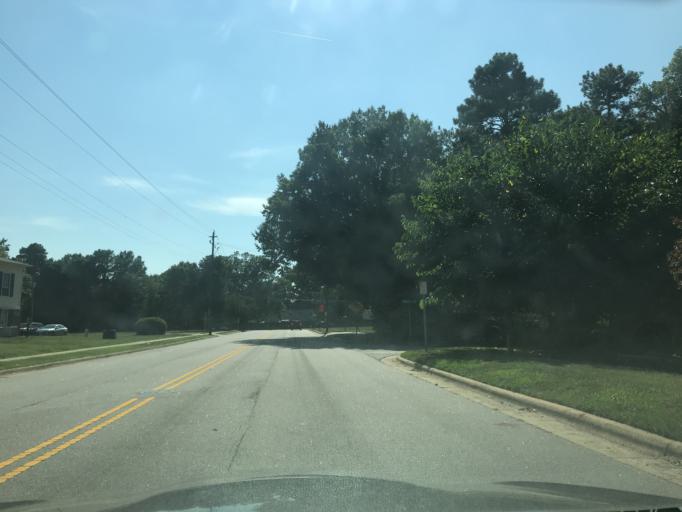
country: US
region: North Carolina
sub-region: Wake County
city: West Raleigh
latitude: 35.8536
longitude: -78.6131
